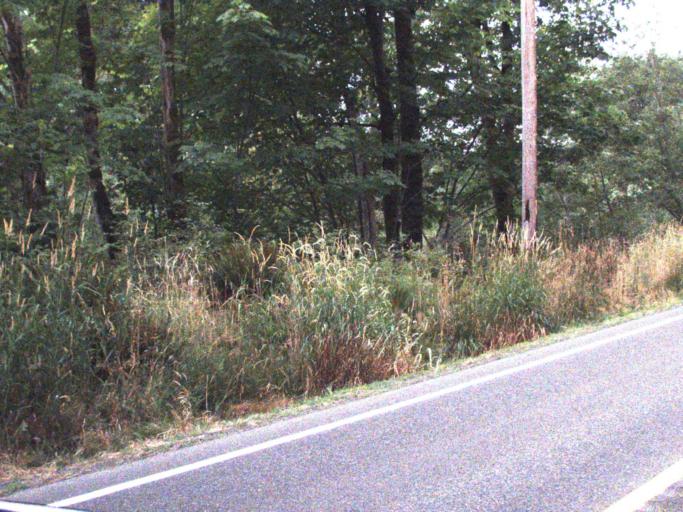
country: US
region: Washington
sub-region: King County
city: Lake Marcel-Stillwater
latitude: 47.6864
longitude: -121.9337
